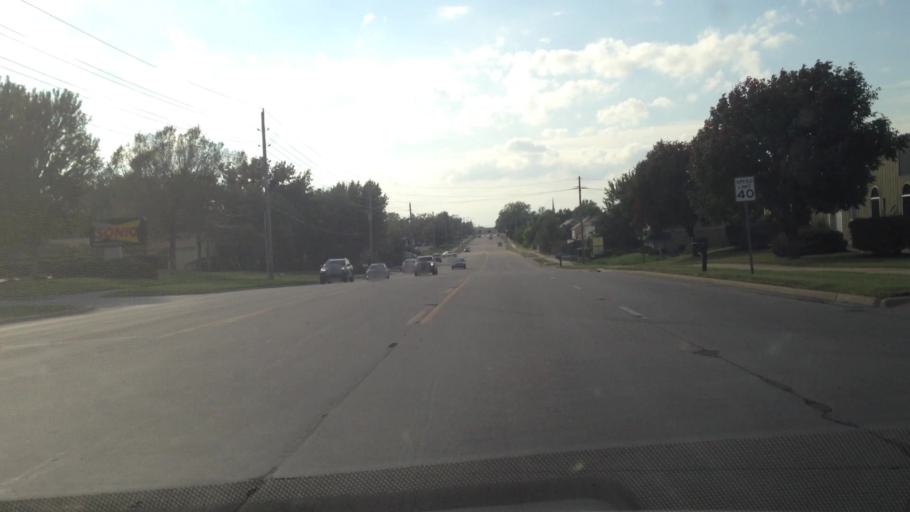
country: US
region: Kansas
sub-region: Douglas County
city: Lawrence
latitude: 38.9282
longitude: -95.2642
